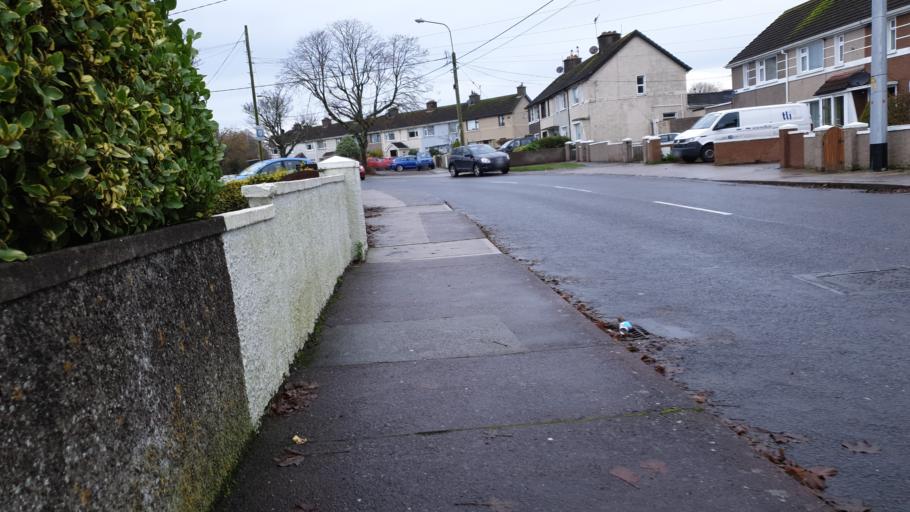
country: IE
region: Munster
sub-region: County Cork
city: Cork
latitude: 51.8915
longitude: -8.4202
